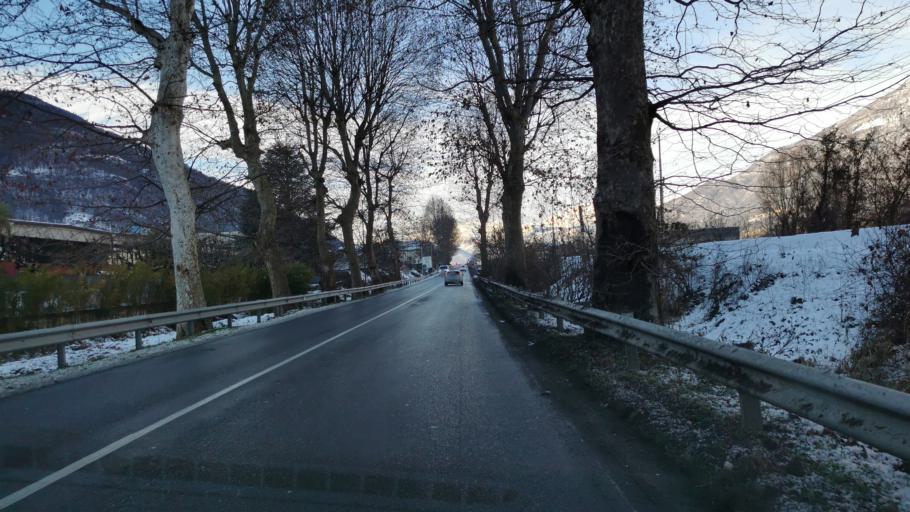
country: IT
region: Lombardy
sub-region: Provincia di Sondrio
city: Regoledo
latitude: 46.1341
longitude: 9.5380
